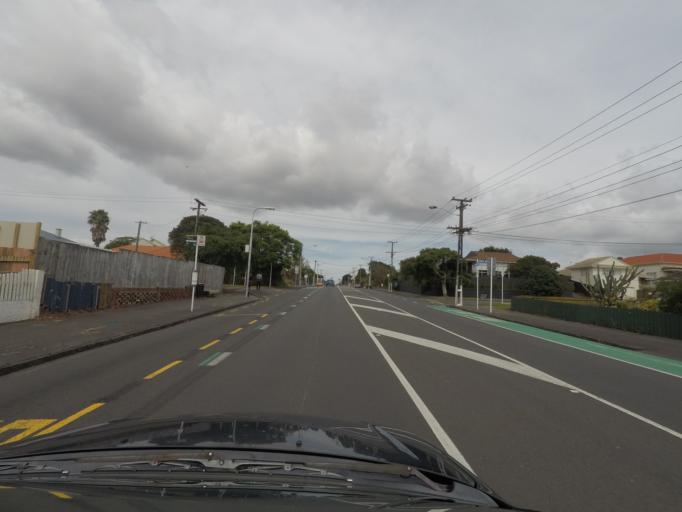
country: NZ
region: Auckland
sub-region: Auckland
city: Auckland
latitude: -36.8825
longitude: 174.7393
